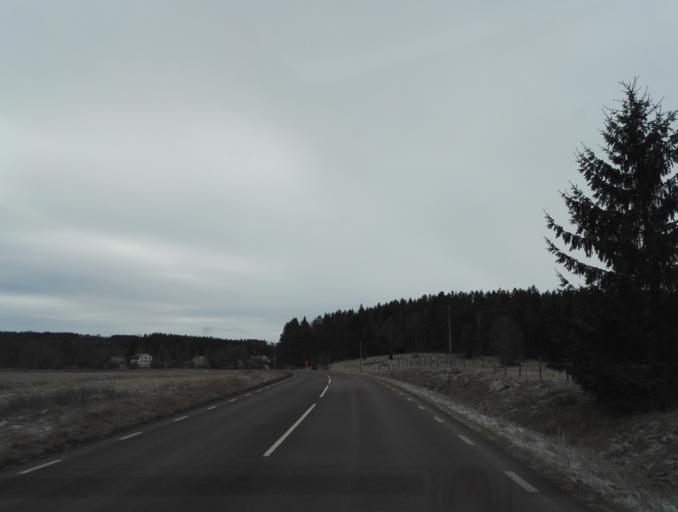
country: SE
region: Kalmar
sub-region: Hultsfreds Kommun
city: Virserum
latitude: 57.3471
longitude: 15.6051
